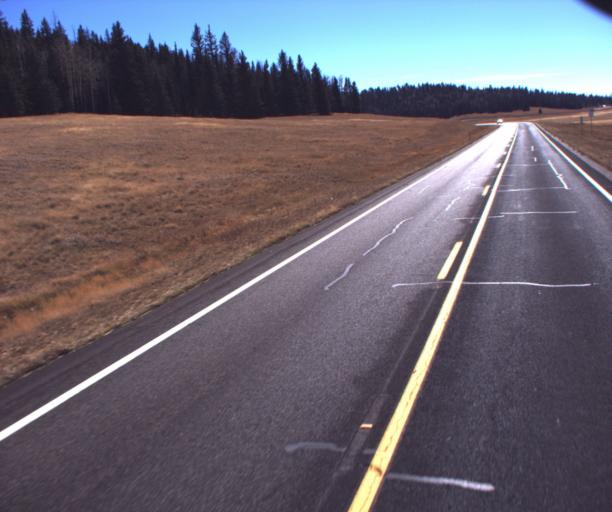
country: US
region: Arizona
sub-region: Coconino County
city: Grand Canyon
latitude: 36.4274
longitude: -112.1318
